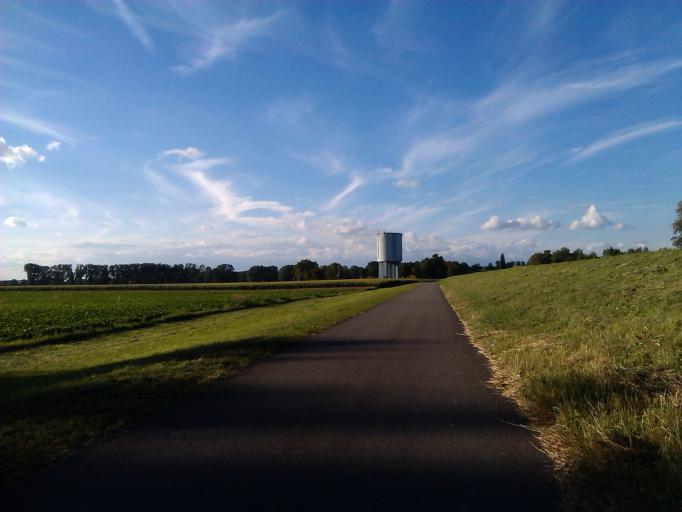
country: DE
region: Rheinland-Pfalz
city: Otterstadt
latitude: 49.3809
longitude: 8.4567
